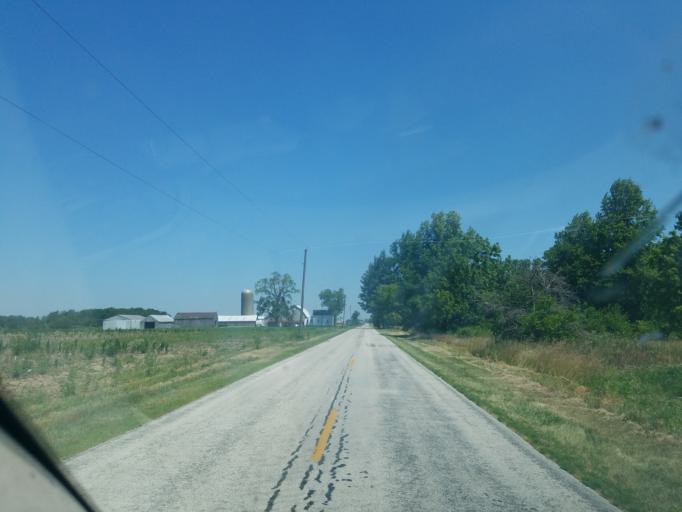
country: US
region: Ohio
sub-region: Mercer County
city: Coldwater
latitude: 40.5699
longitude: -84.7082
